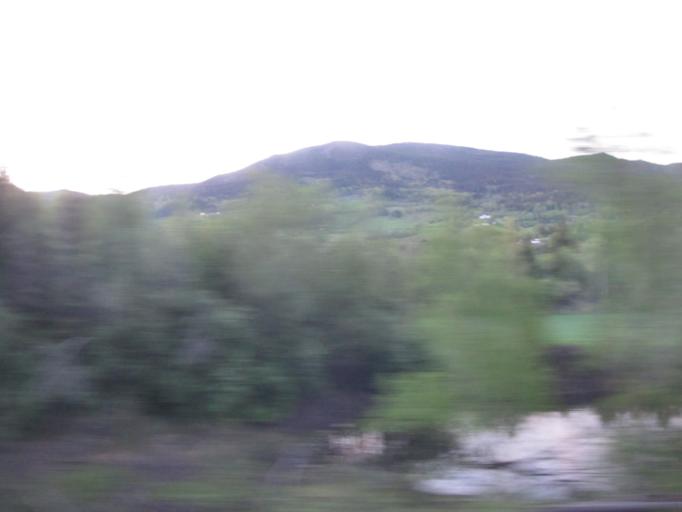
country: NO
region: Oppland
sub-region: Ringebu
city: Ringebu
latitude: 61.4438
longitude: 10.1882
